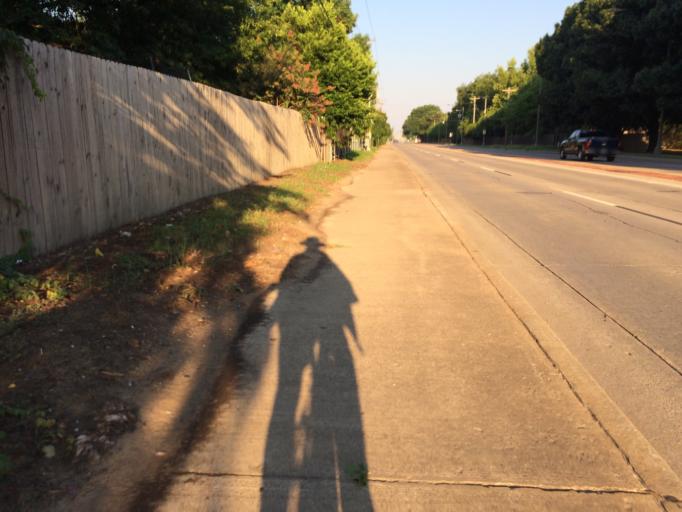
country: US
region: Oklahoma
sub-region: Cleveland County
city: Norman
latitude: 35.2184
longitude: -97.4637
